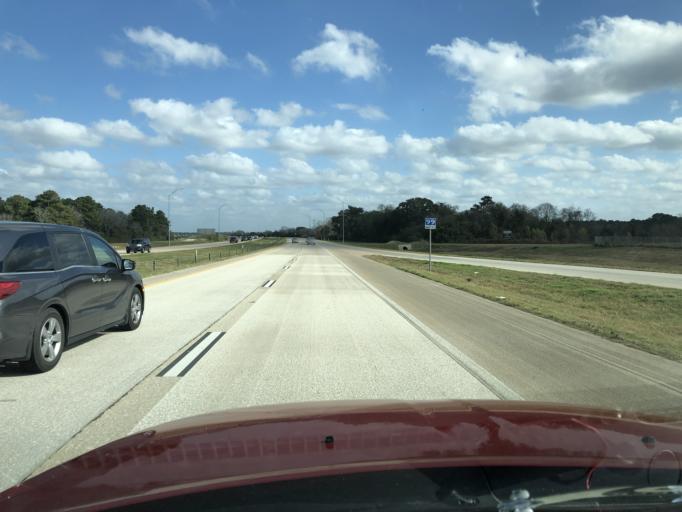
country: US
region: Texas
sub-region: Harris County
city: Cypress
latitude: 30.0513
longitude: -95.6941
